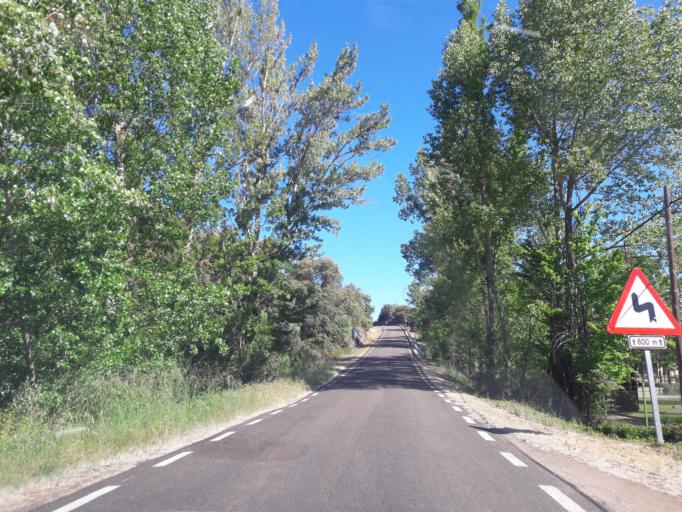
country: ES
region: Castille and Leon
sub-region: Provincia de Salamanca
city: Juzbado
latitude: 41.0679
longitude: -5.8994
